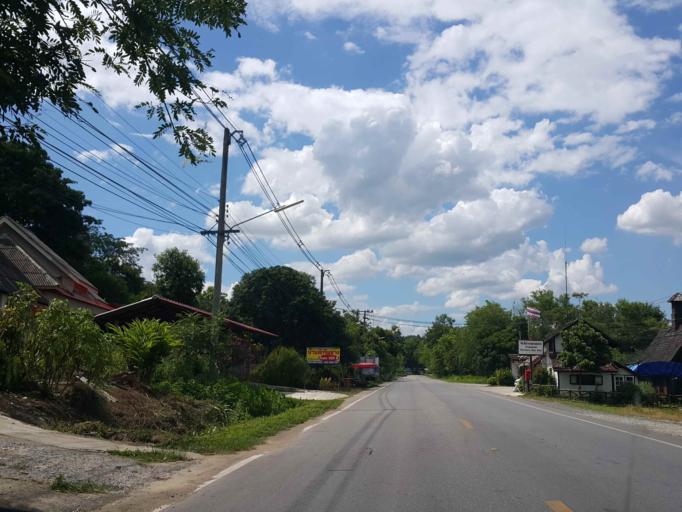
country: TH
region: Chiang Mai
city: Chiang Mai
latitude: 18.9108
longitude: 98.9060
